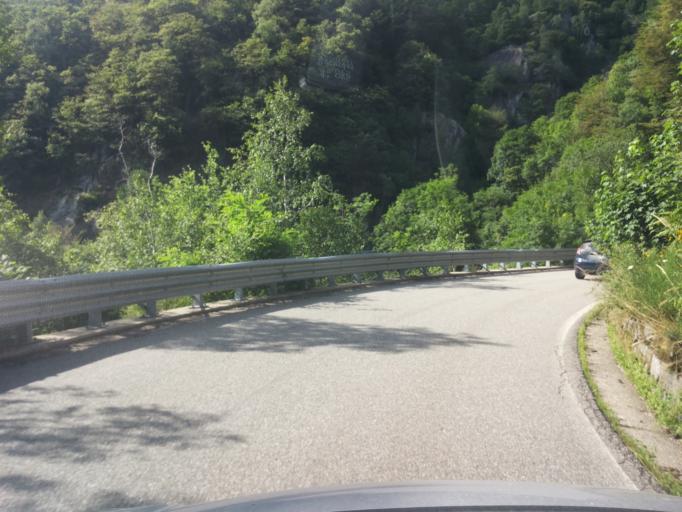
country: IT
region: Piedmont
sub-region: Provincia di Biella
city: Quittengo
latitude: 45.6652
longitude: 8.0114
